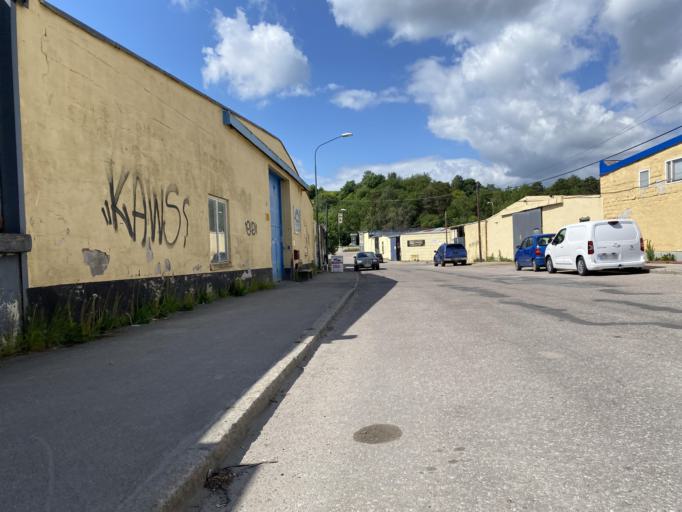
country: SE
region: Stockholm
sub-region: Jarfalla Kommun
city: Jakobsberg
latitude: 59.3751
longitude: 17.8550
